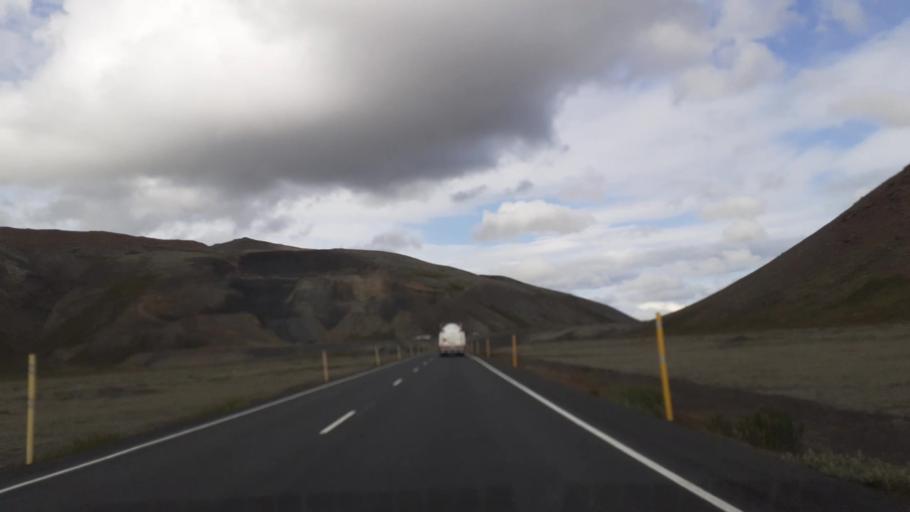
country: IS
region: South
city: THorlakshoefn
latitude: 64.0026
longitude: -21.4609
